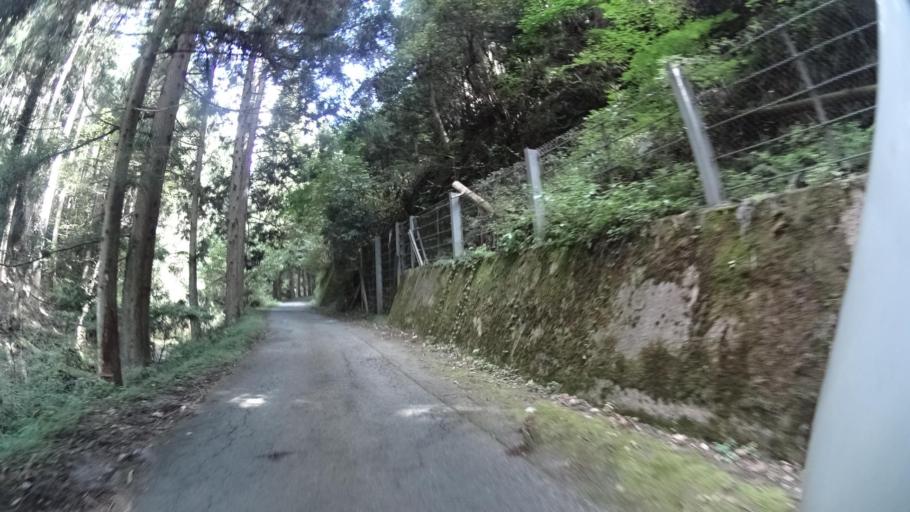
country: JP
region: Kyoto
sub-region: Kyoto-shi
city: Kamigyo-ku
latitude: 35.1344
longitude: 135.7642
